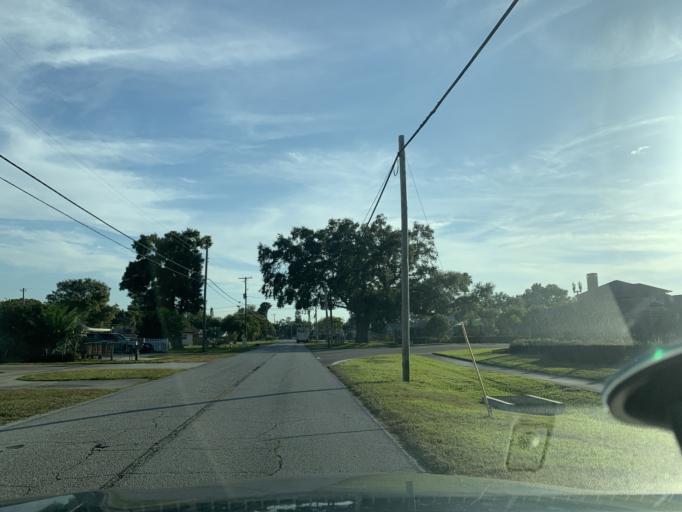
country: US
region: Florida
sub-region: Pinellas County
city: Ridgecrest
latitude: 27.8847
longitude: -82.7978
